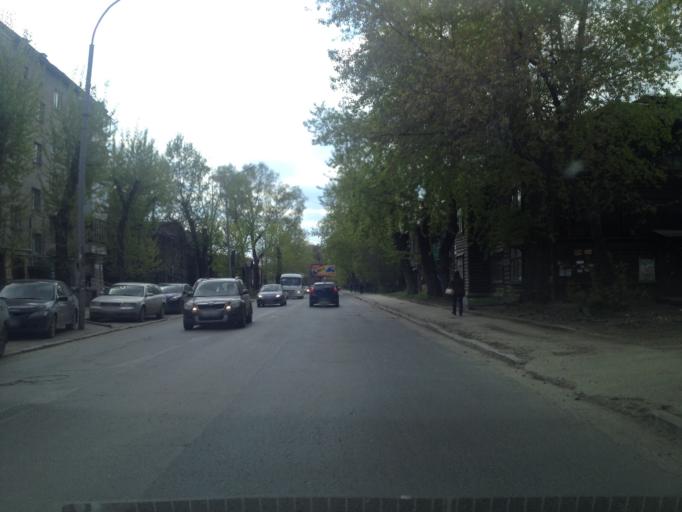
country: RU
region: Sverdlovsk
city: Yekaterinburg
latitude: 56.8572
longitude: 60.5933
